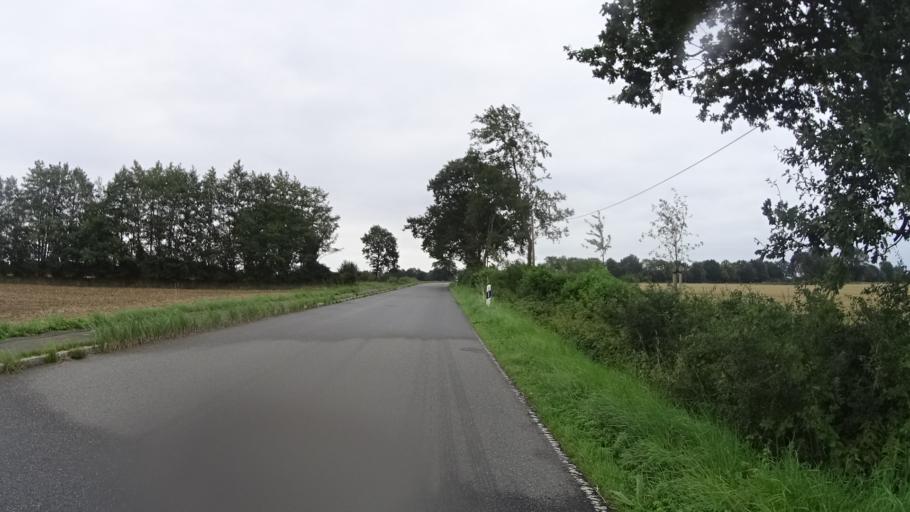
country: DE
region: Schleswig-Holstein
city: Lasbek
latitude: 53.7381
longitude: 10.3469
